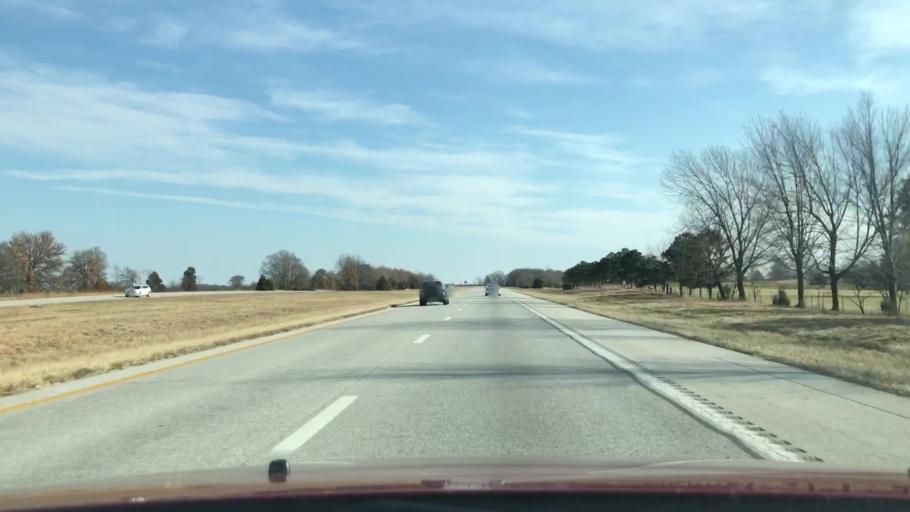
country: US
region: Missouri
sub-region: Webster County
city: Rogersville
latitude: 37.1234
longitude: -92.9913
